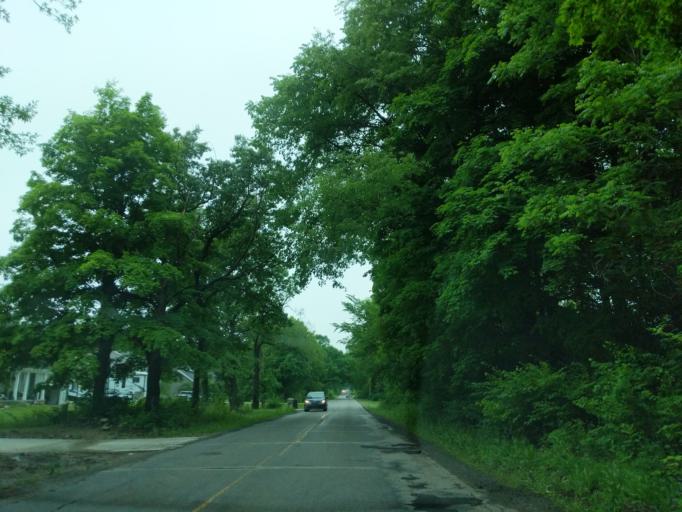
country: US
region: Michigan
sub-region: Jackson County
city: Spring Arbor
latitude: 42.2184
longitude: -84.5465
